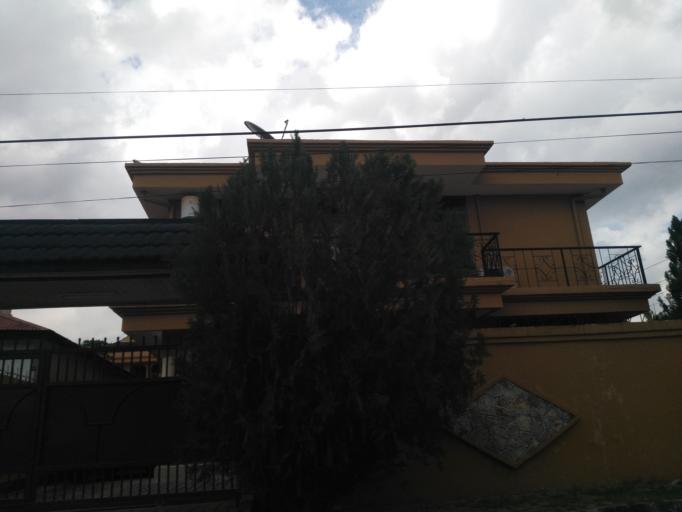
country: TZ
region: Dar es Salaam
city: Magomeni
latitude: -6.7627
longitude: 39.2465
